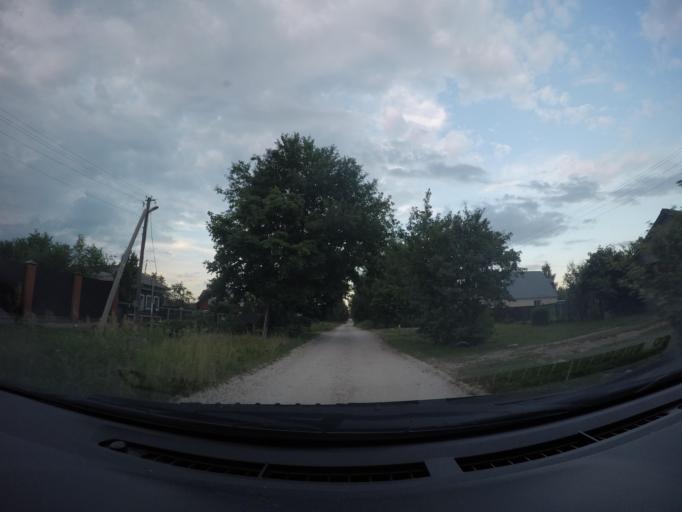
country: RU
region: Moskovskaya
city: Krasnyy Tkach
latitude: 55.3854
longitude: 39.2090
